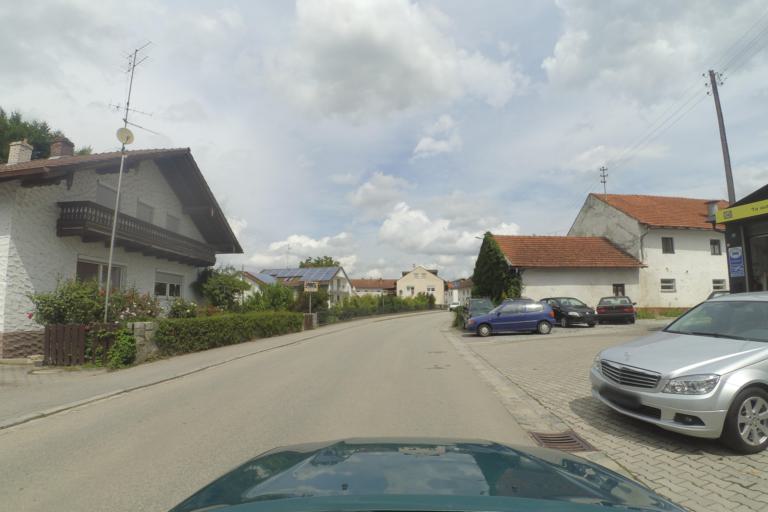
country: DE
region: Bavaria
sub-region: Lower Bavaria
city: Mamming
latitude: 48.6530
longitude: 12.6049
